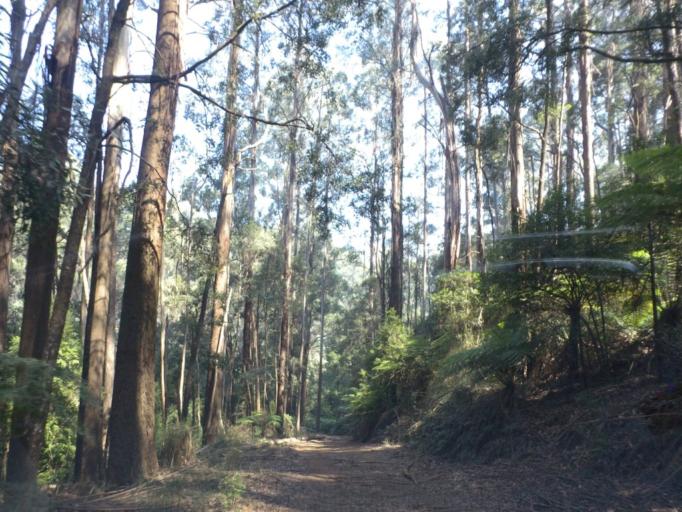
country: AU
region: Victoria
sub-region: Yarra Ranges
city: Healesville
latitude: -37.5658
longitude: 145.6150
